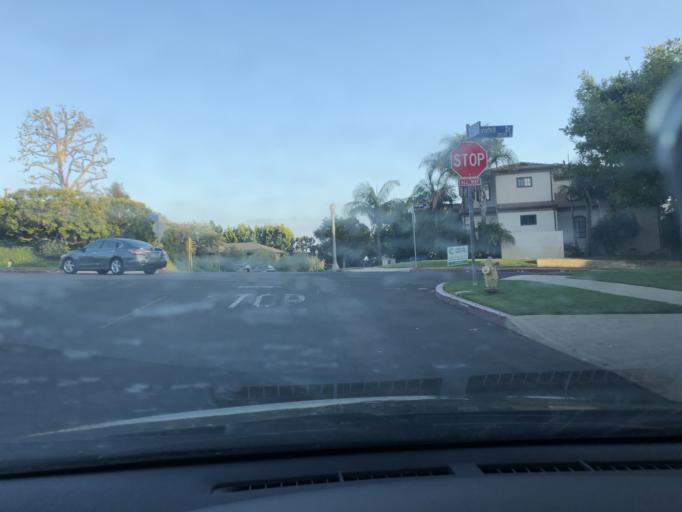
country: US
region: California
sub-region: Los Angeles County
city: Culver City
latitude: 34.0378
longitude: -118.4017
